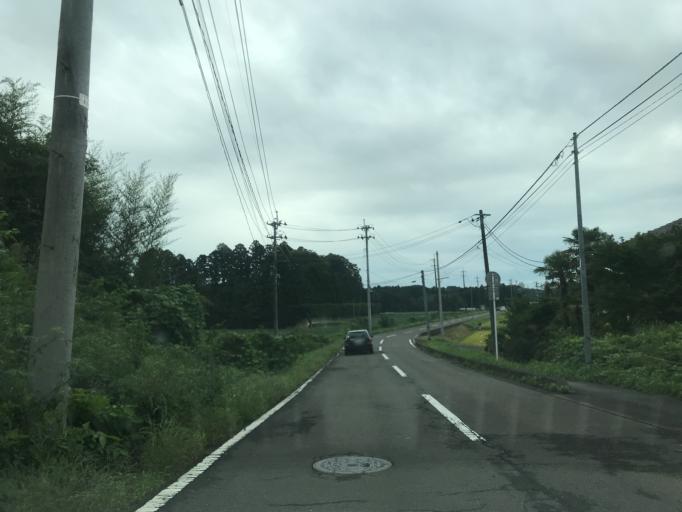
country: JP
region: Miyagi
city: Sendai-shi
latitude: 38.3241
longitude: 140.8632
